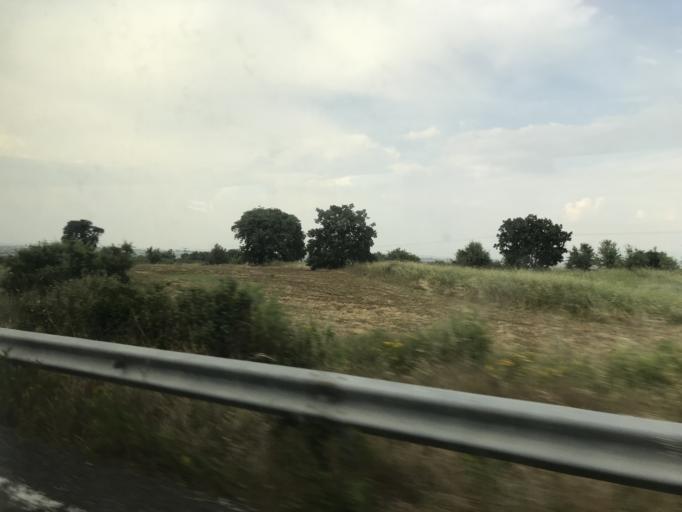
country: GR
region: East Macedonia and Thrace
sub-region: Nomos Rodopis
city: Sapes
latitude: 40.9587
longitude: 25.6474
